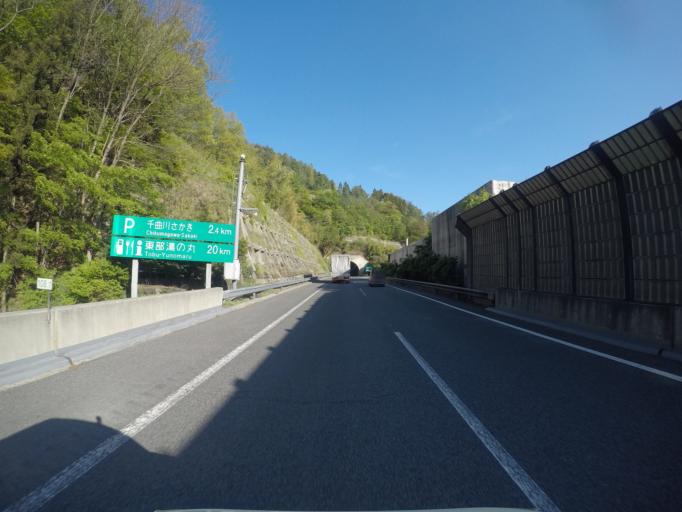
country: JP
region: Nagano
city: Ueda
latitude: 36.4781
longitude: 138.1921
